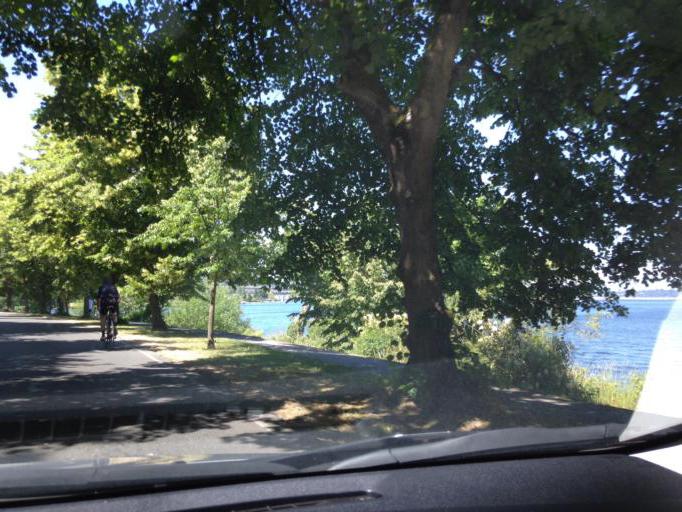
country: US
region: Washington
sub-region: King County
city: Seattle
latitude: 47.5807
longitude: -122.2847
